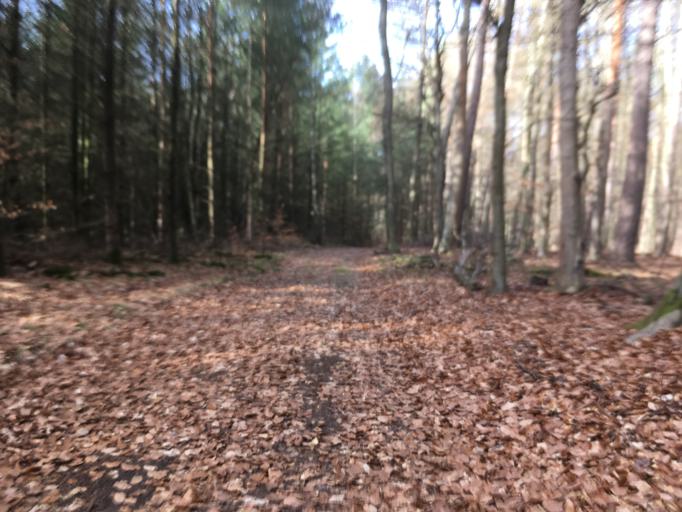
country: DE
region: Brandenburg
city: Wandlitz
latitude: 52.7302
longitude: 13.5237
